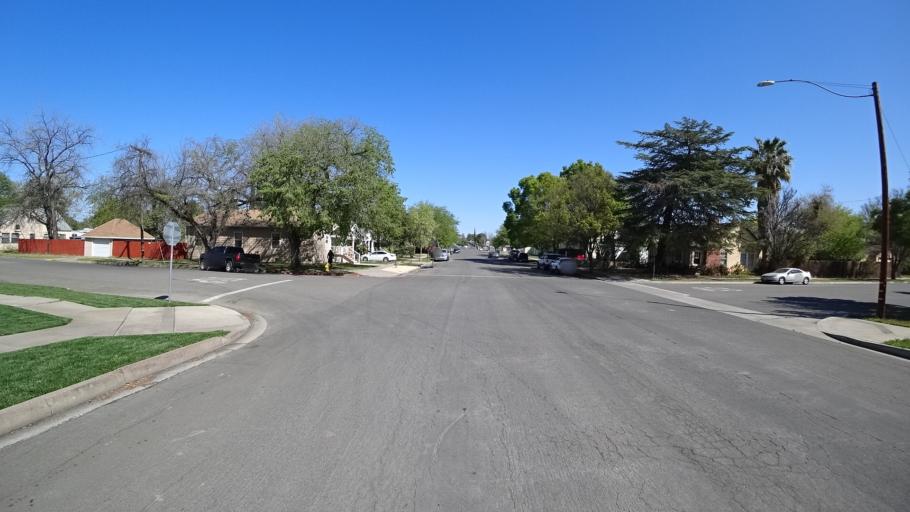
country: US
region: California
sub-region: Glenn County
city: Willows
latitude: 39.5216
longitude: -122.2032
